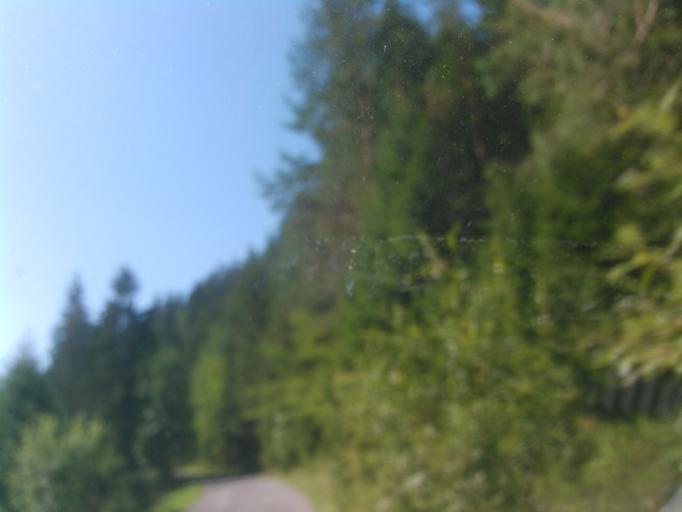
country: SK
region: Zilinsky
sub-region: Okres Liptovsky Mikulas
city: Liptovsky Mikulas
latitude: 49.0191
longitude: 19.5207
